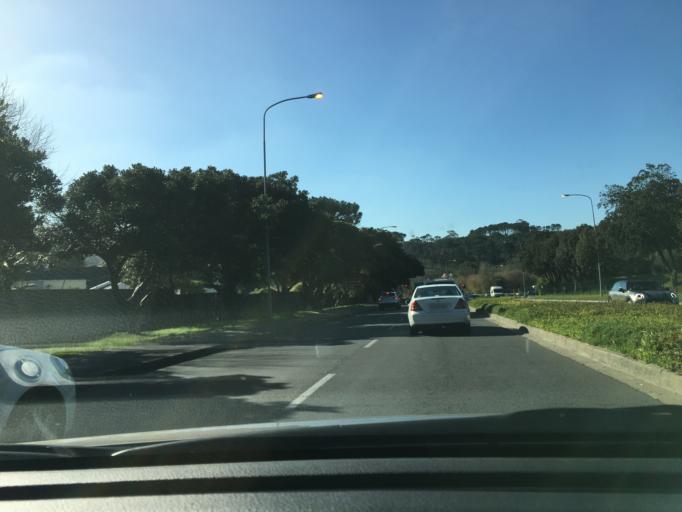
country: ZA
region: Western Cape
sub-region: City of Cape Town
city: Bergvliet
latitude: -34.0160
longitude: 18.4505
